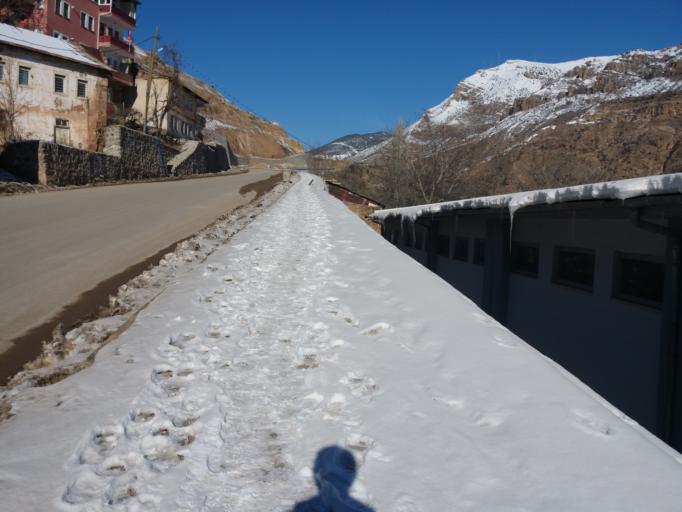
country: TR
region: Gumushane
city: Gumushkhane
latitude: 40.4403
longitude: 39.5020
